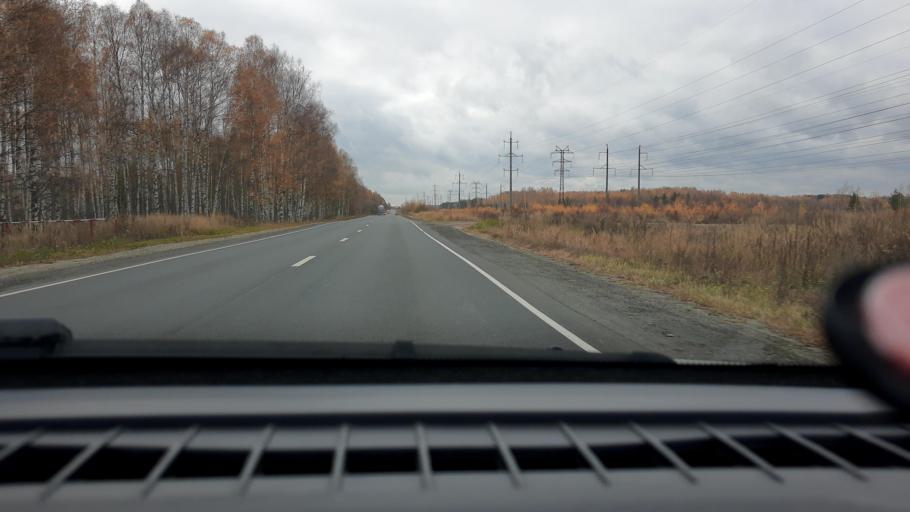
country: RU
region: Nizjnij Novgorod
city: Lukino
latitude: 56.3564
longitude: 43.5921
